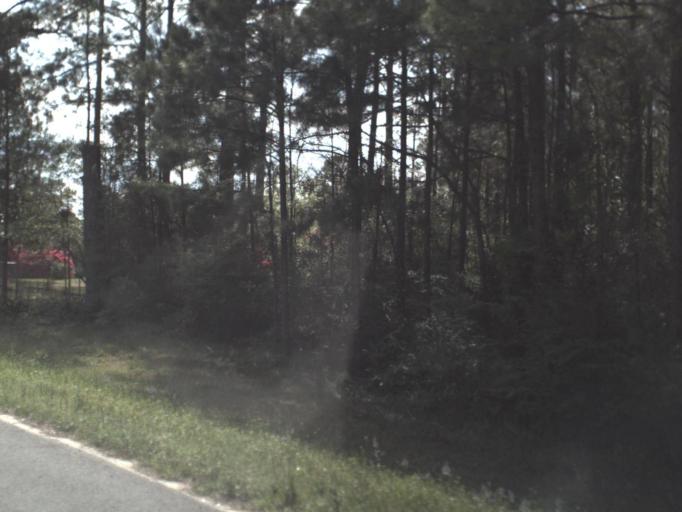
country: US
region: Alabama
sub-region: Covington County
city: Florala
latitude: 30.9644
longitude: -86.4627
